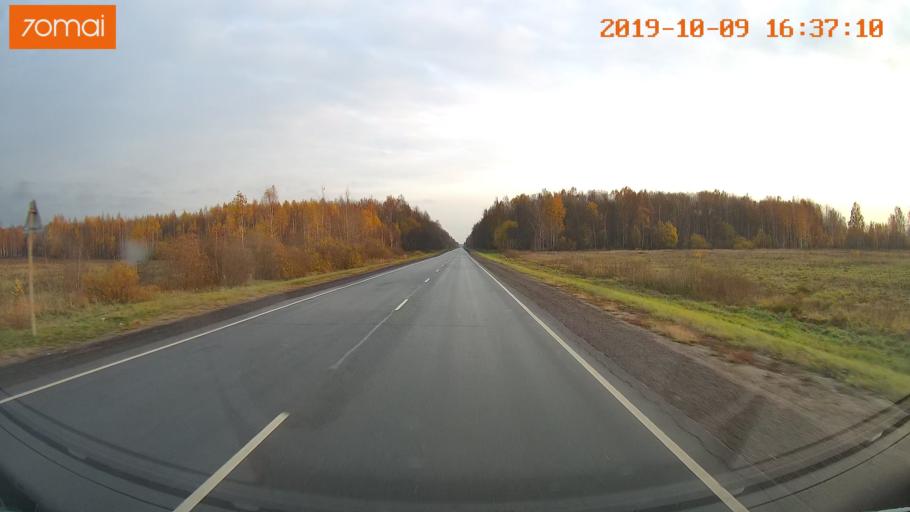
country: RU
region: Kostroma
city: Volgorechensk
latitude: 57.5310
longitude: 41.0213
